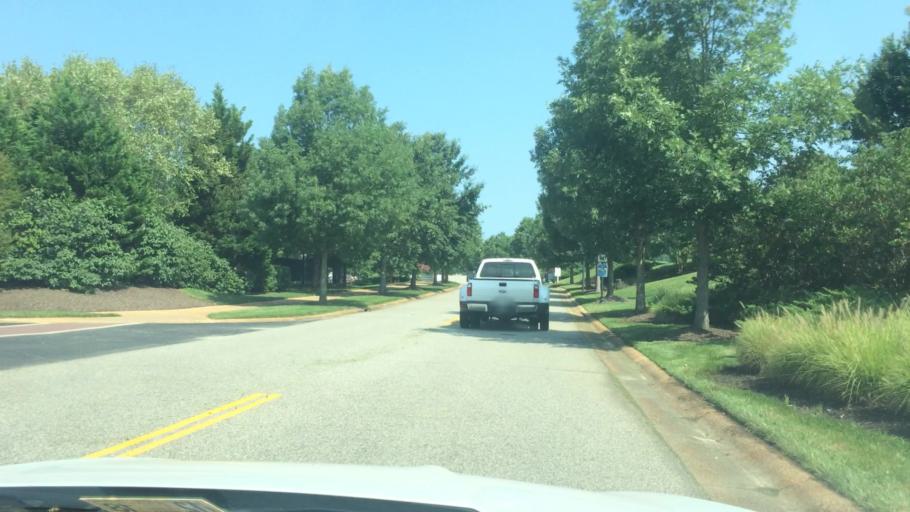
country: US
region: Virginia
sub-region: James City County
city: Williamsburg
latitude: 37.3519
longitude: -76.7692
